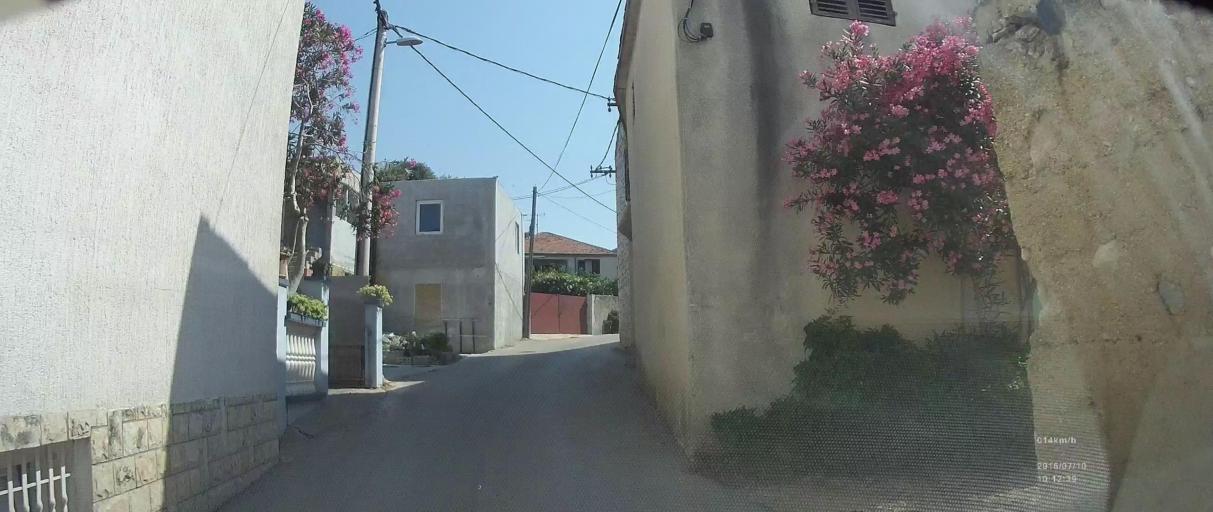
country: HR
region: Zadarska
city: Pakostane
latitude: 43.9087
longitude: 15.5109
